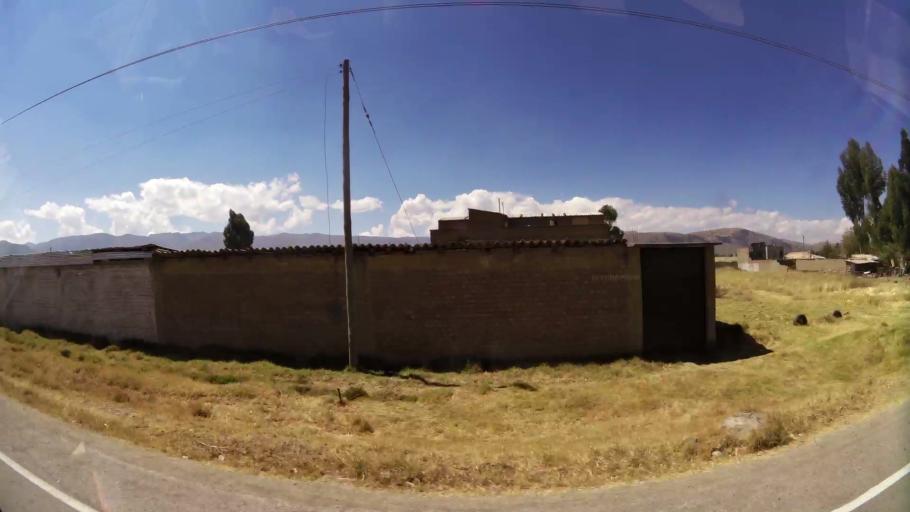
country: PE
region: Junin
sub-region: Provincia de Jauja
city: Jauja
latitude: -11.7664
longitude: -75.4941
